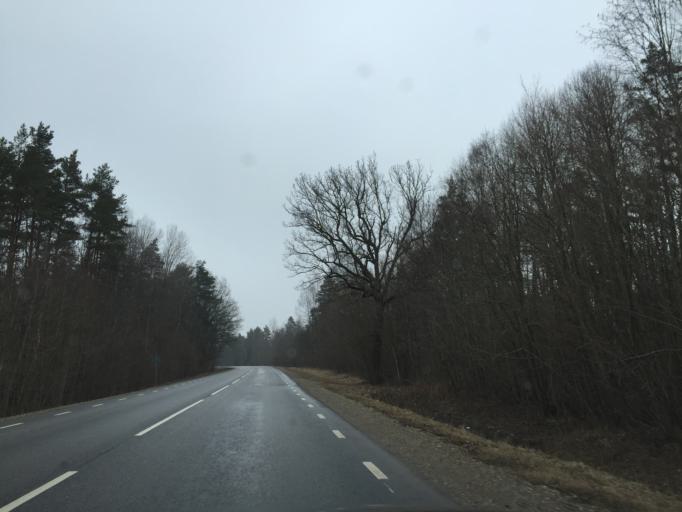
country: EE
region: Laeaene
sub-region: Lihula vald
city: Lihula
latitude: 58.6089
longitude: 23.6958
